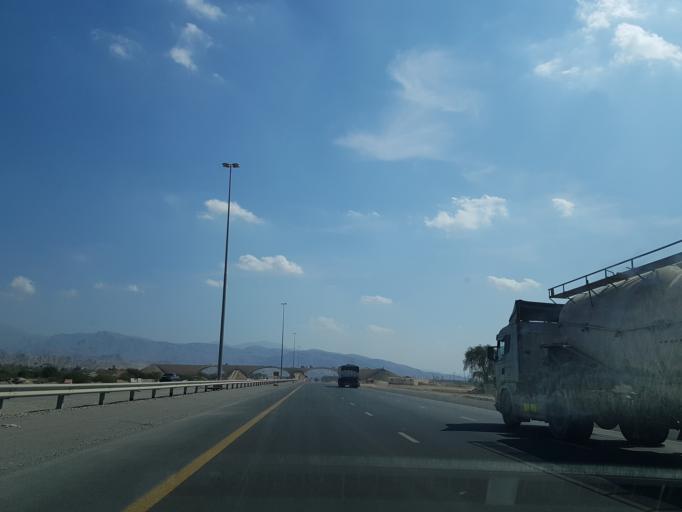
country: AE
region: Ra's al Khaymah
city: Ras al-Khaimah
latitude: 25.8241
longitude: 56.0228
